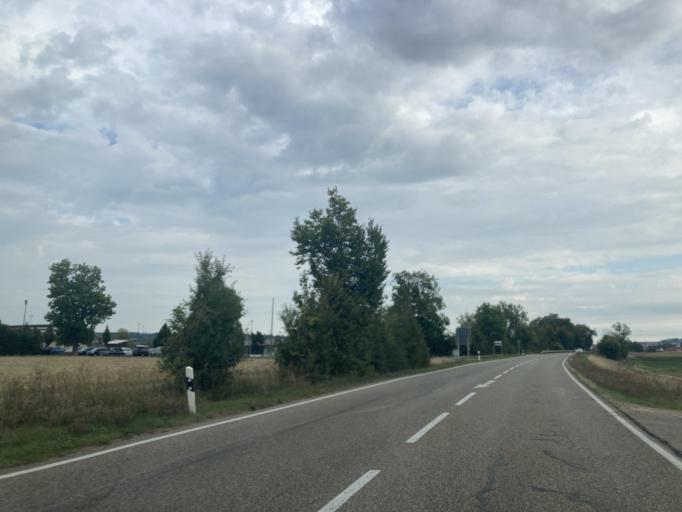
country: DE
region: Bavaria
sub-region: Swabia
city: Oettingen in Bayern
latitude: 48.9400
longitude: 10.5891
